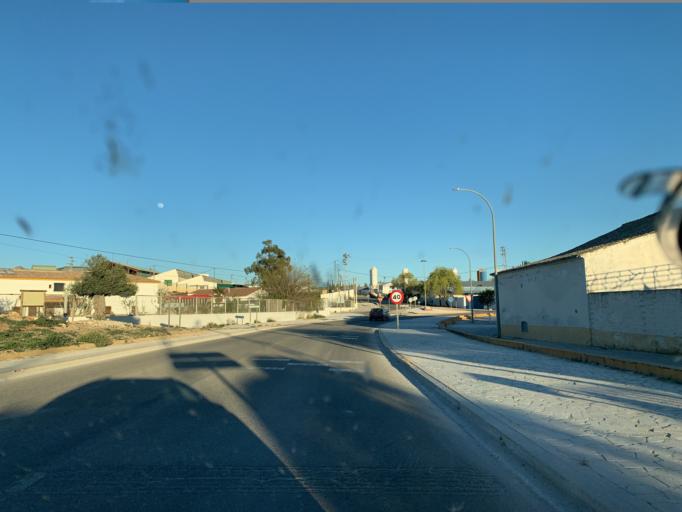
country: ES
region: Andalusia
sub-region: Provincia de Sevilla
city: Pedrera
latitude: 37.2302
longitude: -4.8940
